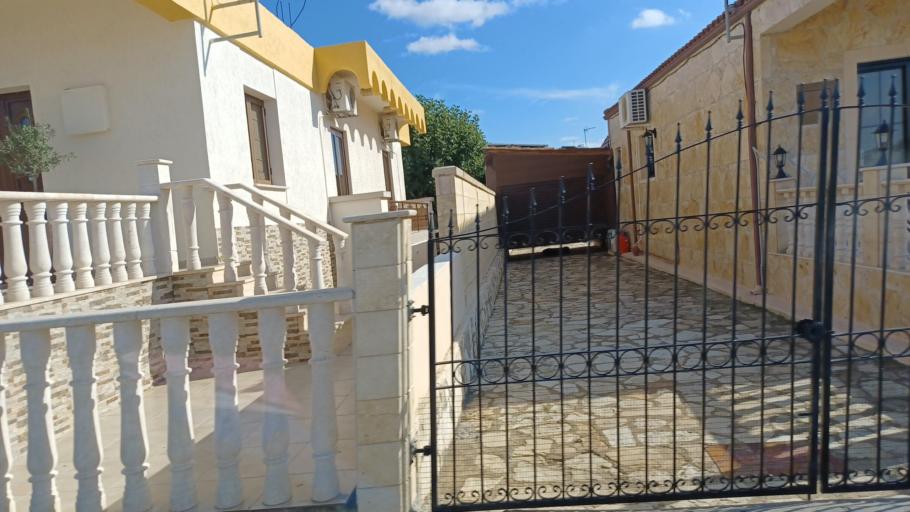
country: CY
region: Larnaka
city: Troulloi
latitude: 35.0315
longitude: 33.6131
